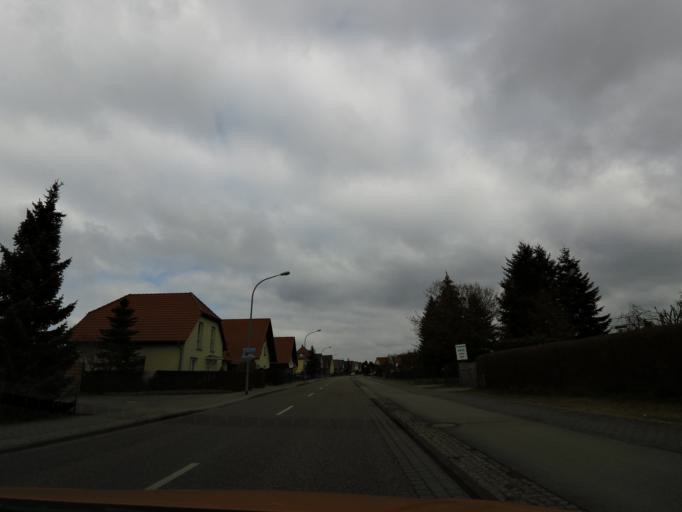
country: DE
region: Brandenburg
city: Rathenow
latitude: 52.6193
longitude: 12.3427
